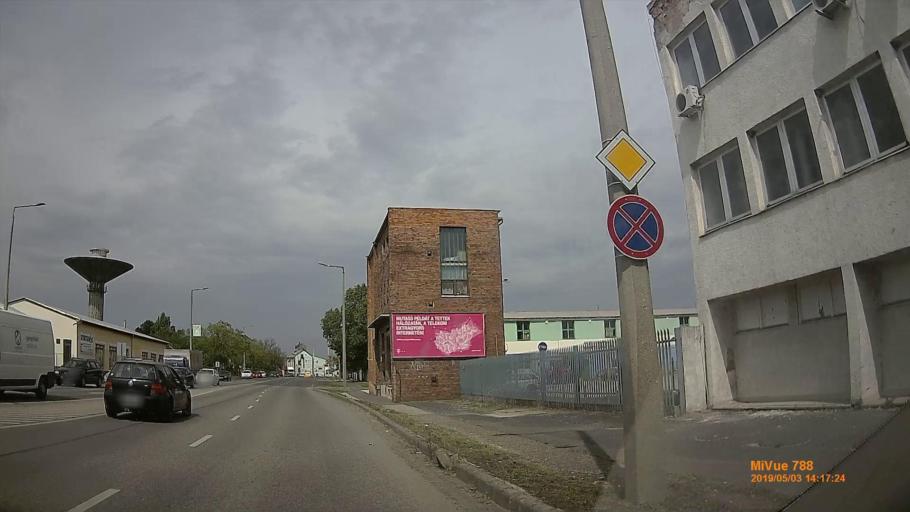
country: HU
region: Jasz-Nagykun-Szolnok
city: Szolnok
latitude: 47.1604
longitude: 20.1742
